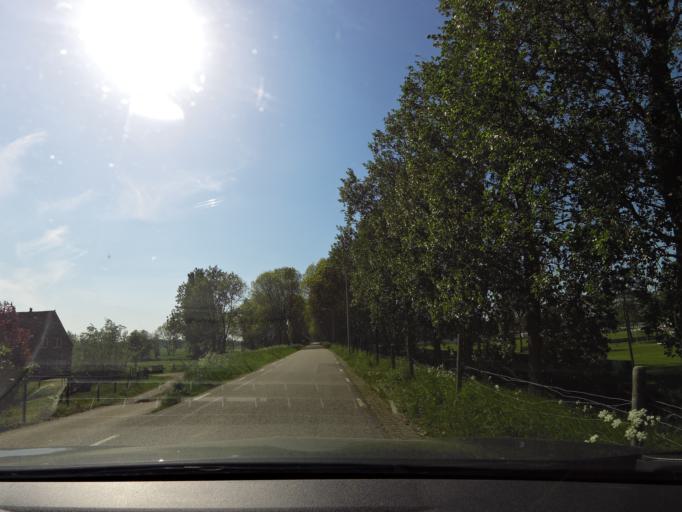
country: NL
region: South Holland
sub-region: Gemeente Albrandswaard
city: Rhoon
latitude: 51.8509
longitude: 4.4388
